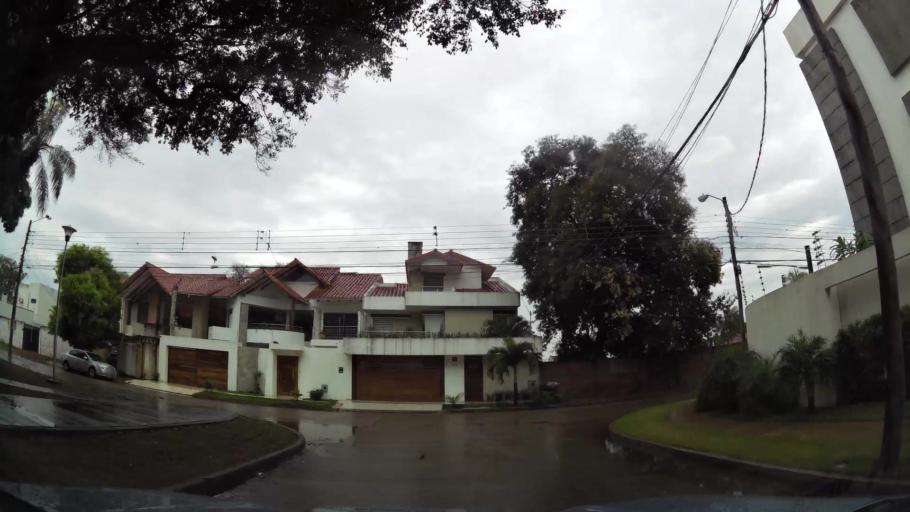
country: BO
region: Santa Cruz
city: Santa Cruz de la Sierra
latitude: -17.8050
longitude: -63.1707
